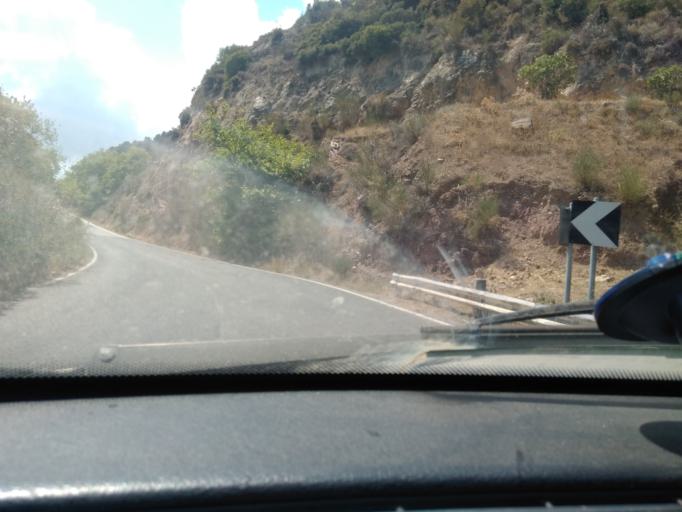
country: GR
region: Crete
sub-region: Nomos Lasithiou
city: Siteia
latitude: 35.1295
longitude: 26.0659
